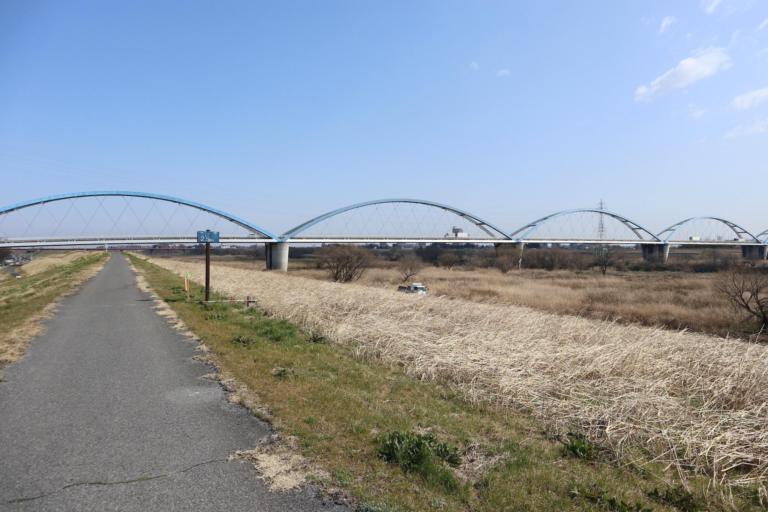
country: JP
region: Ibaraki
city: Koga
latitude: 36.1825
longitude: 139.6887
